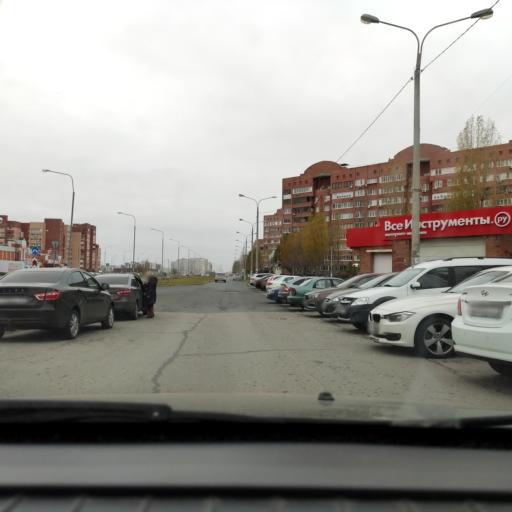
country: RU
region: Samara
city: Tol'yatti
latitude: 53.5383
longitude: 49.3565
